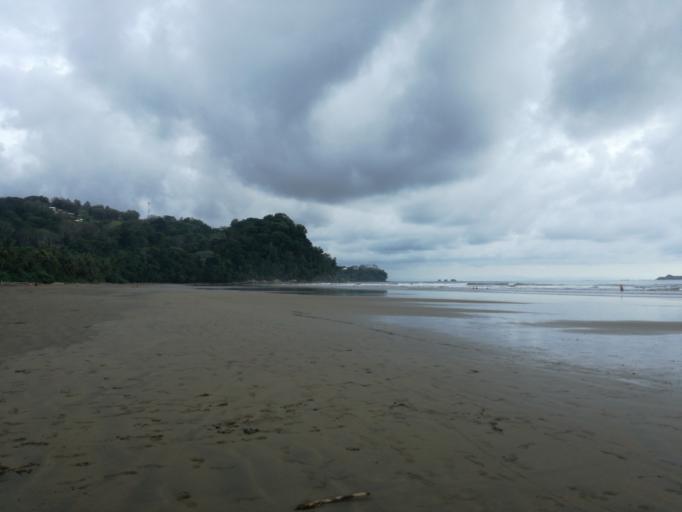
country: CR
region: San Jose
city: Mercedes
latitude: 9.1483
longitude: -83.7325
